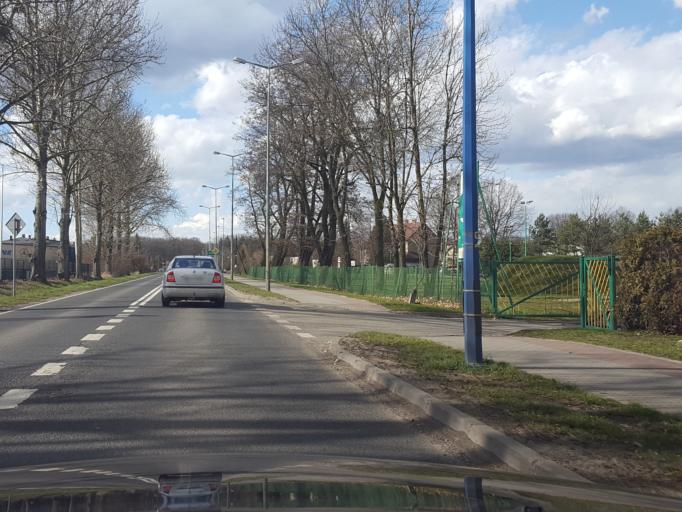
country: PL
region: Silesian Voivodeship
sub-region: Powiat pszczynski
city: Kobior
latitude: 50.0633
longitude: 18.9209
